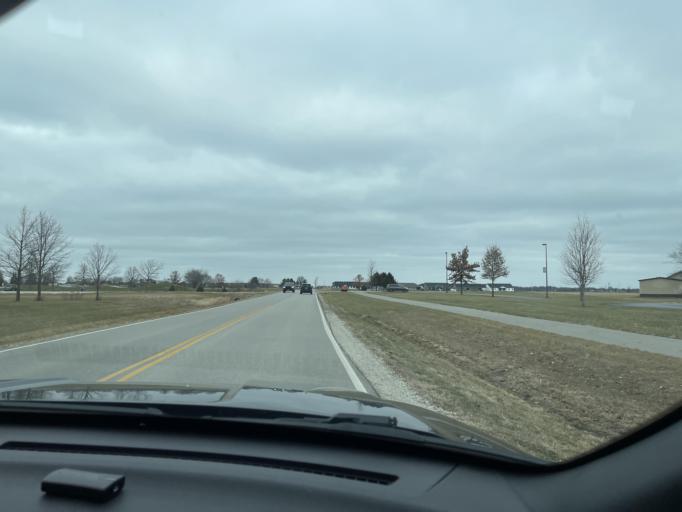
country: US
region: Illinois
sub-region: Sangamon County
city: Jerome
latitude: 39.7577
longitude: -89.7532
